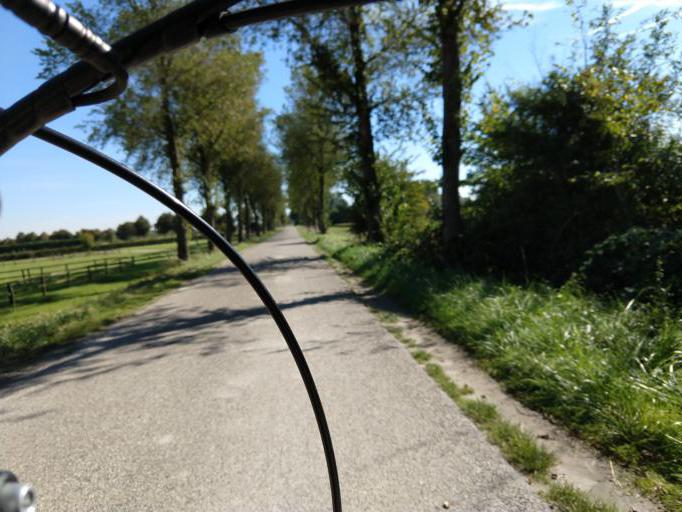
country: NL
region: Zeeland
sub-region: Gemeente Goes
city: Goes
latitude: 51.4362
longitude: 3.8359
